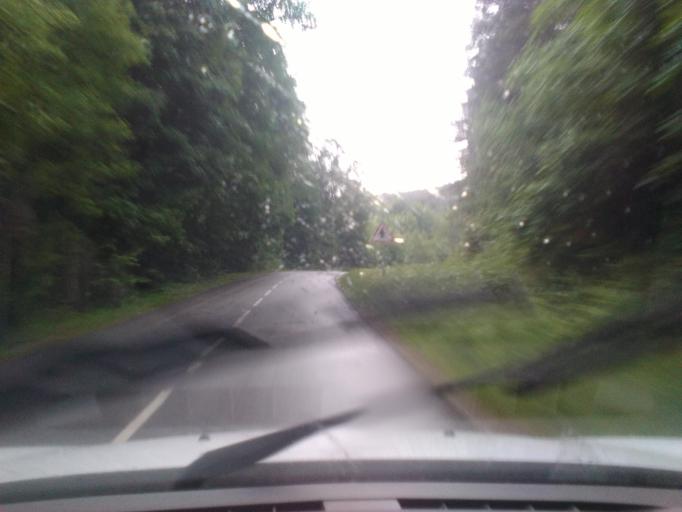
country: FR
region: Lorraine
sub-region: Departement des Vosges
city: Bruyeres
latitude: 48.2652
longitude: 6.7252
